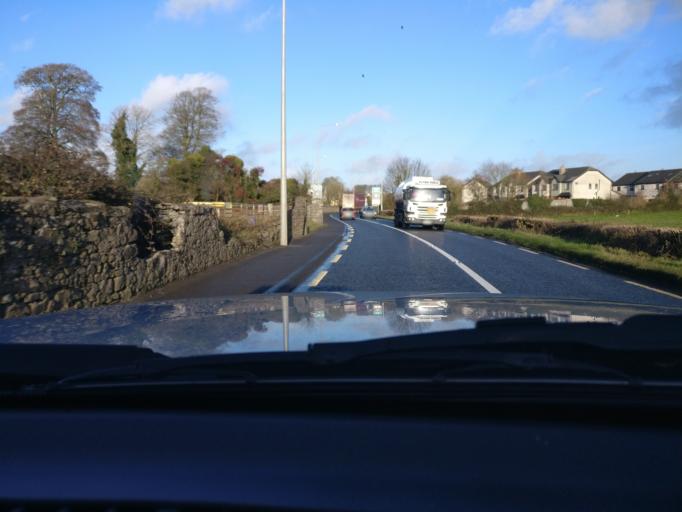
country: IE
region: Leinster
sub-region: An Iarmhi
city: Rathwire
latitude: 53.6081
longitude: -7.0979
